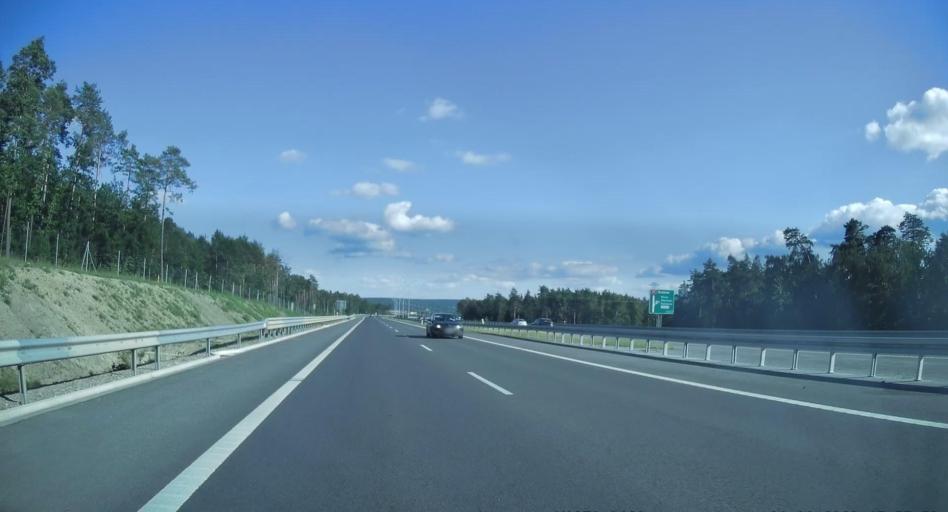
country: PL
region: Swietokrzyskie
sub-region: Powiat skarzyski
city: Skarzysko-Kamienna
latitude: 51.1271
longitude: 20.8412
